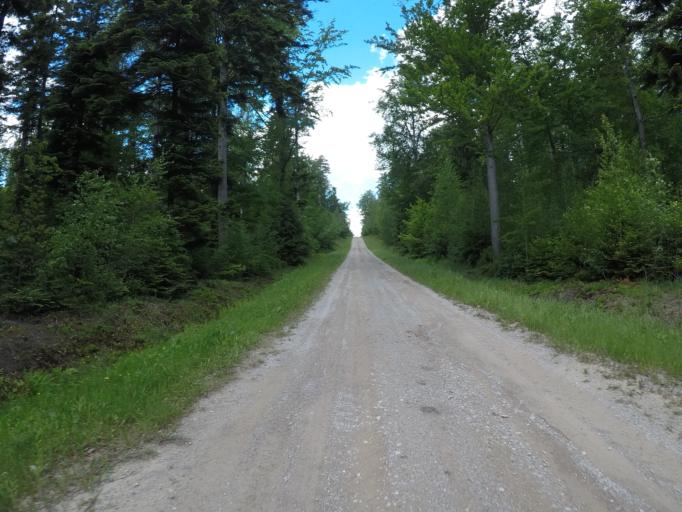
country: PL
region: Swietokrzyskie
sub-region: Powiat kielecki
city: Kostomloty Pierwsze
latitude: 50.9328
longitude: 20.6249
